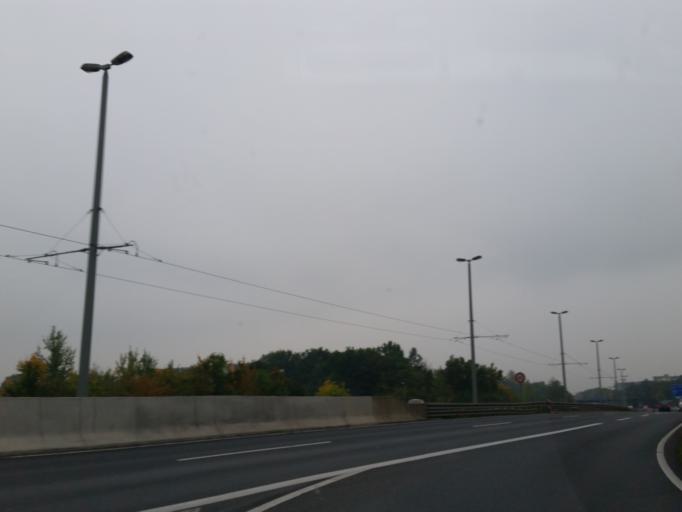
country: DE
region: Lower Saxony
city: Braunschweig
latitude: 52.2379
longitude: 10.5277
